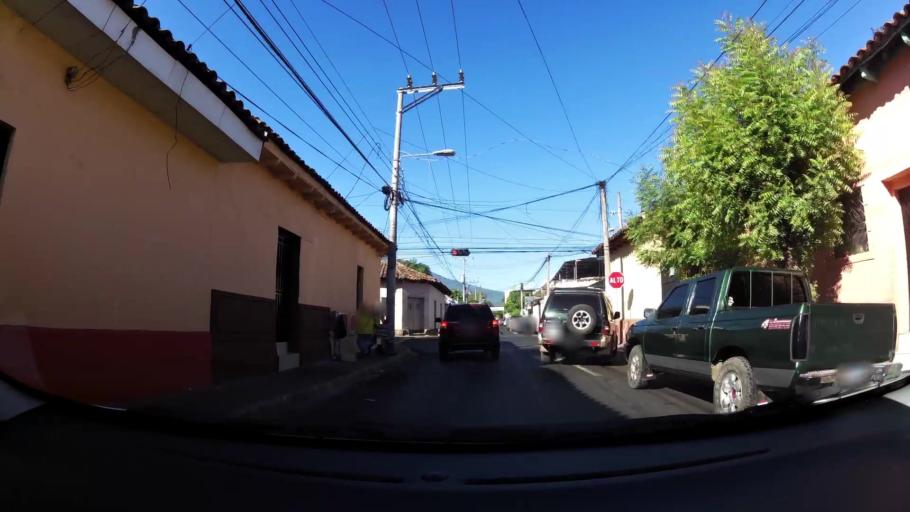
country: SV
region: San Miguel
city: San Miguel
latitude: 13.4767
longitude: -88.1801
